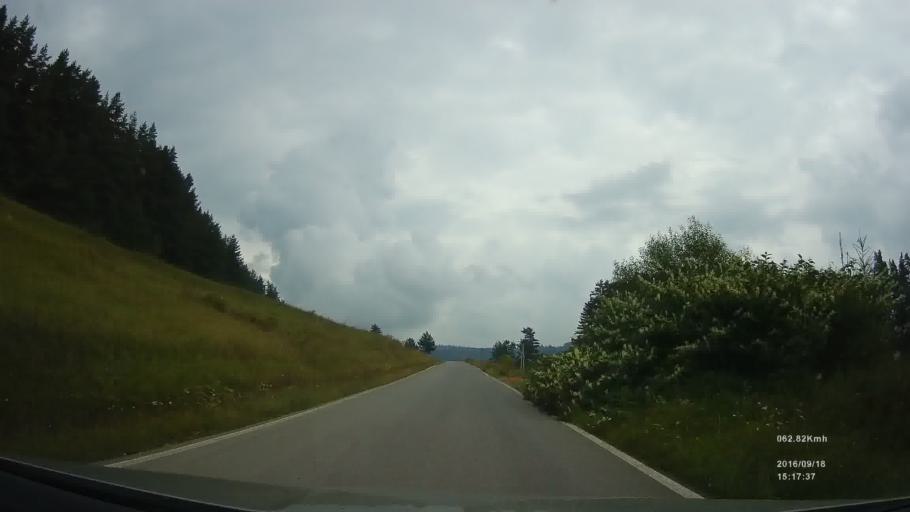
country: SK
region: Presovsky
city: Lubica
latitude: 49.0240
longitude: 20.4905
